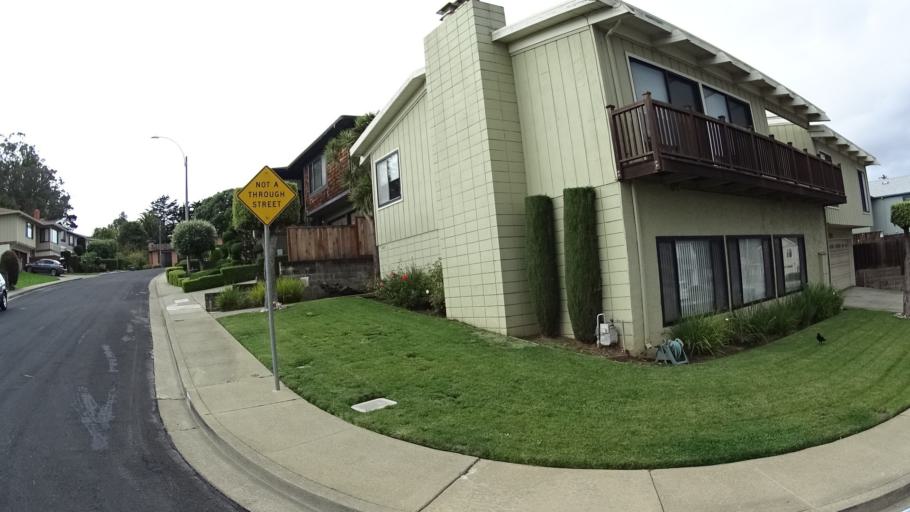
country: US
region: California
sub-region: San Mateo County
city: San Bruno
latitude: 37.6391
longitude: -122.4357
